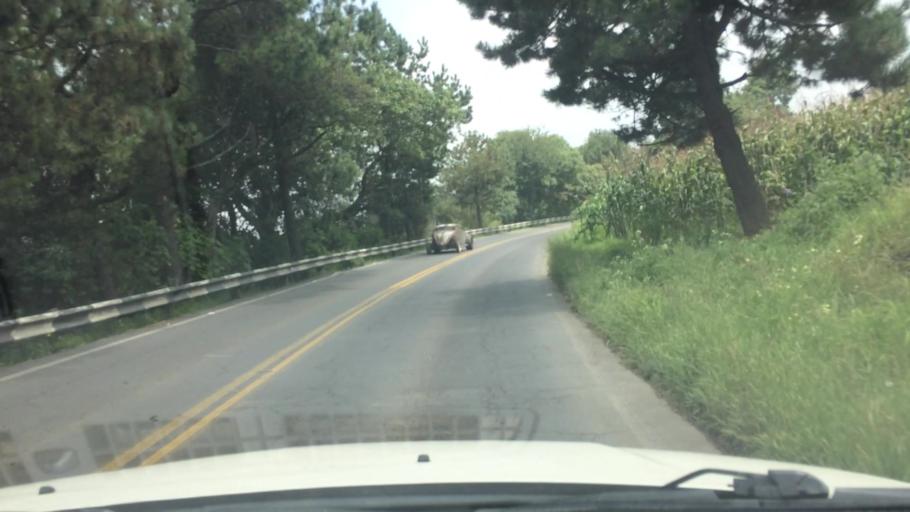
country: MX
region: Mexico City
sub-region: Tlalpan
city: Lomas de Tepemecatl
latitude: 19.2313
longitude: -99.2159
